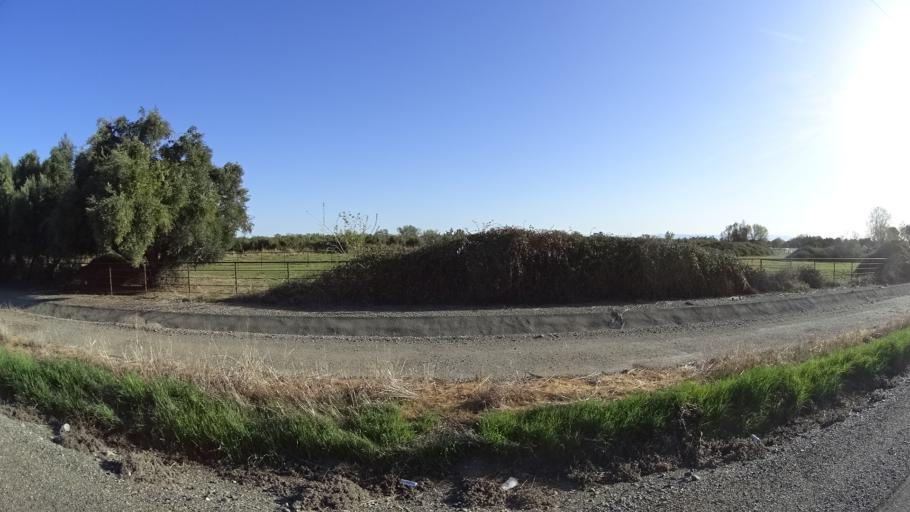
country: US
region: California
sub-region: Glenn County
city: Orland
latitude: 39.7651
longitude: -122.2426
